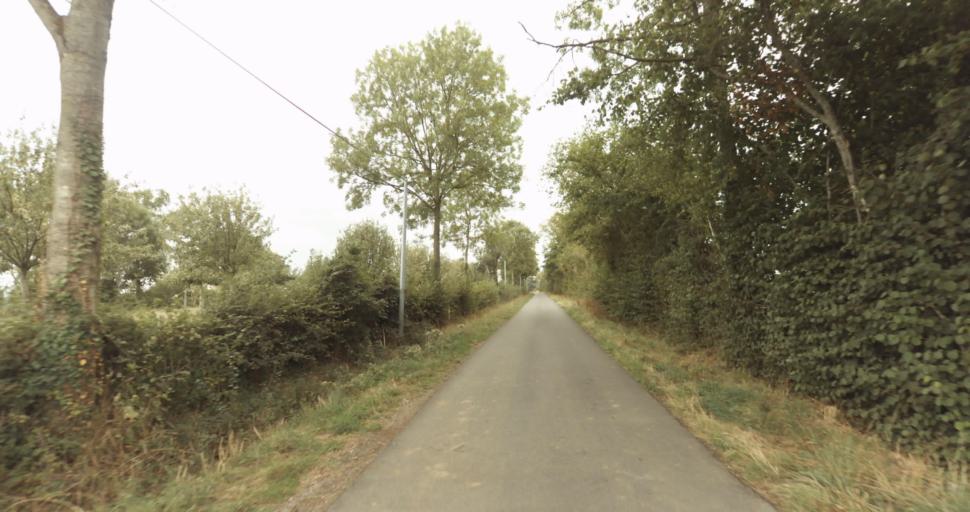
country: FR
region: Lower Normandy
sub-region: Departement de l'Orne
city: Gace
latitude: 48.8716
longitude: 0.2974
